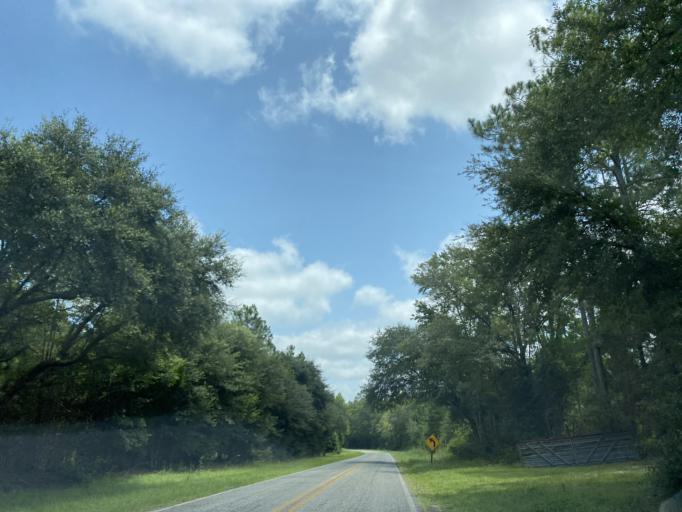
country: US
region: Georgia
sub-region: Wheeler County
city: Alamo
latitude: 32.0801
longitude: -82.7500
